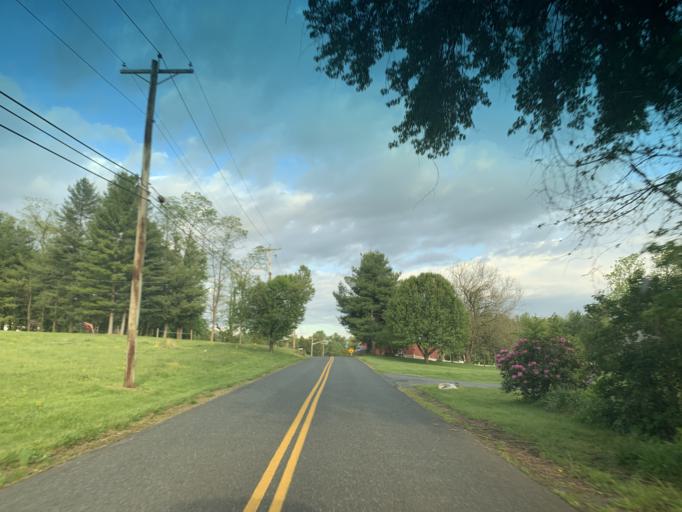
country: US
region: Pennsylvania
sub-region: York County
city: Susquehanna Trails
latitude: 39.6717
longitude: -76.2324
